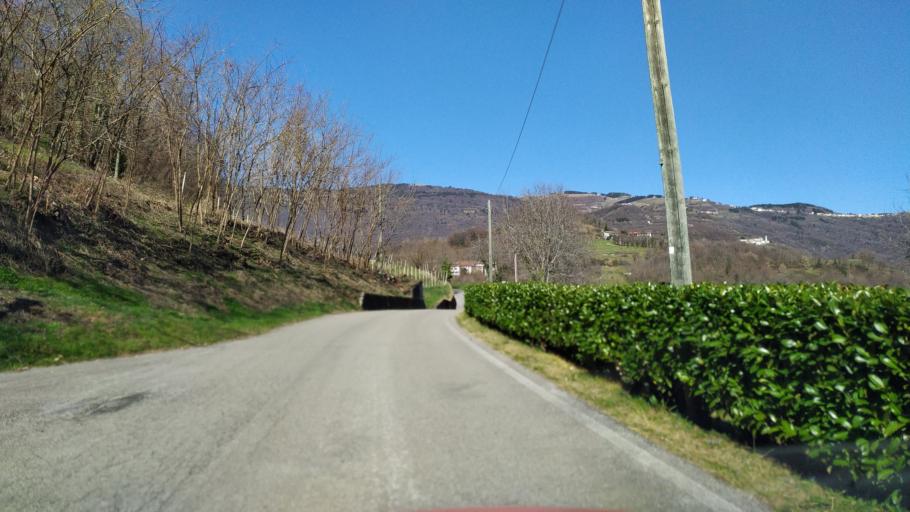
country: IT
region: Veneto
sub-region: Provincia di Vicenza
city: Fara Vicentino
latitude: 45.7578
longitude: 11.5420
